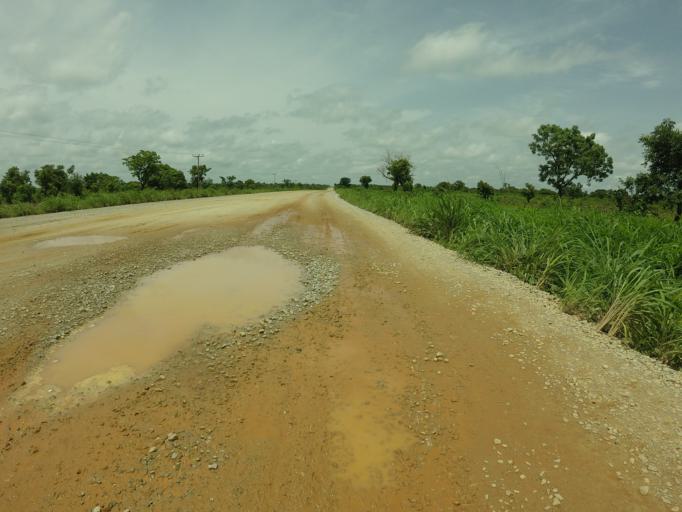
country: GH
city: Kpandae
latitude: 8.5752
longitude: 0.2433
